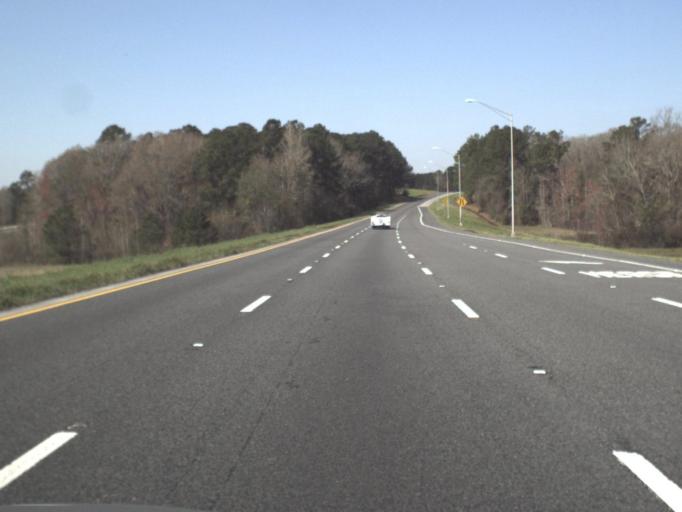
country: US
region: Florida
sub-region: Jackson County
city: Sneads
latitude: 30.6394
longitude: -84.9882
